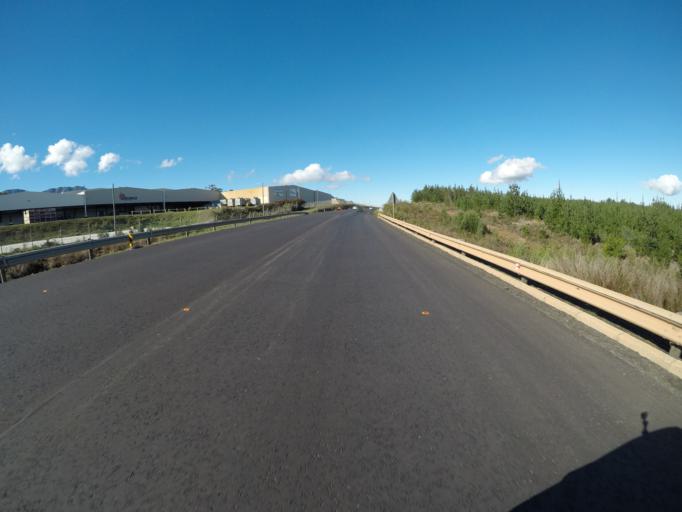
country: ZA
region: Western Cape
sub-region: Overberg District Municipality
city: Grabouw
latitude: -34.1785
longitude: 19.0757
